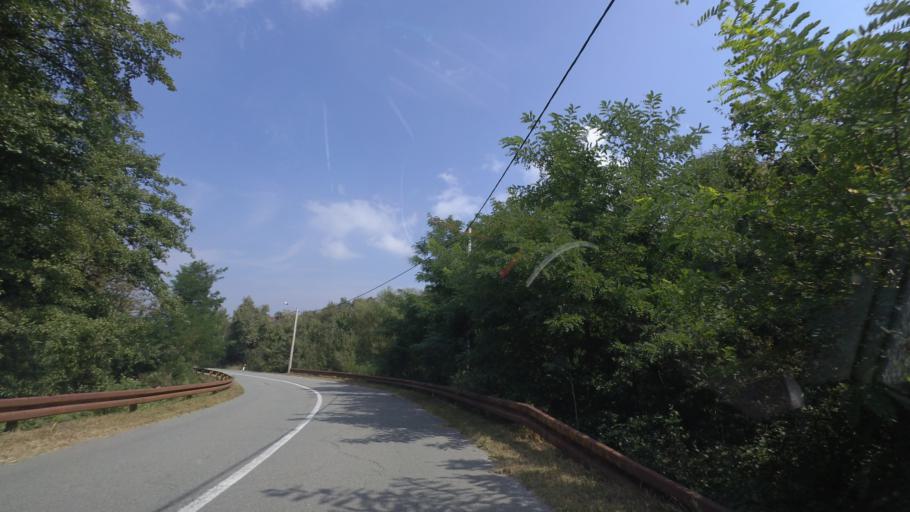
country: BA
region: Federation of Bosnia and Herzegovina
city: Zboriste
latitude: 45.1698
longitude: 16.1358
